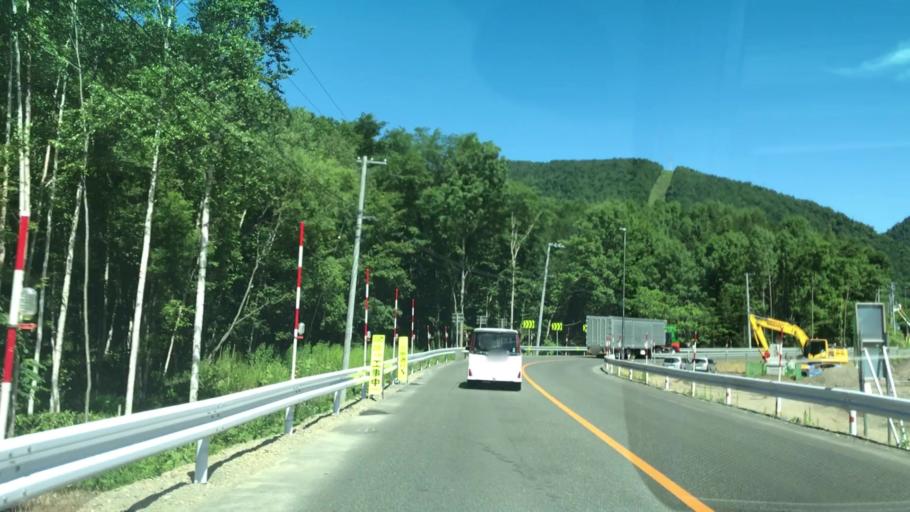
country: JP
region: Hokkaido
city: Shimo-furano
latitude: 42.9242
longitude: 142.5923
